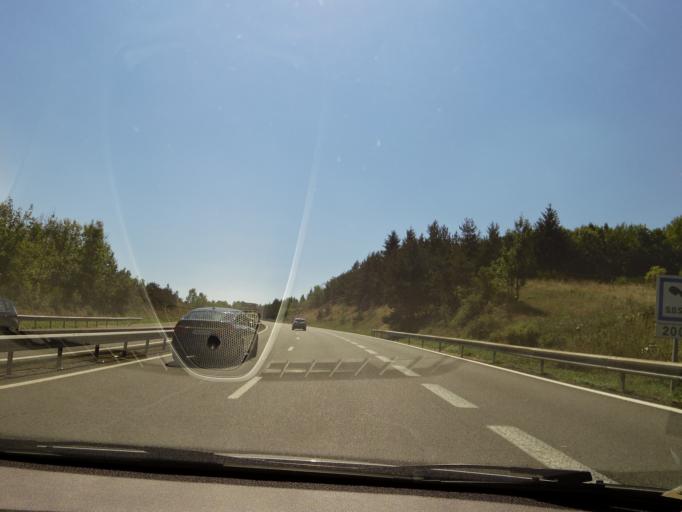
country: FR
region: Rhone-Alpes
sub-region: Departement de la Loire
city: Saint-Just-en-Chevalet
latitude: 45.8653
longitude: 3.8252
